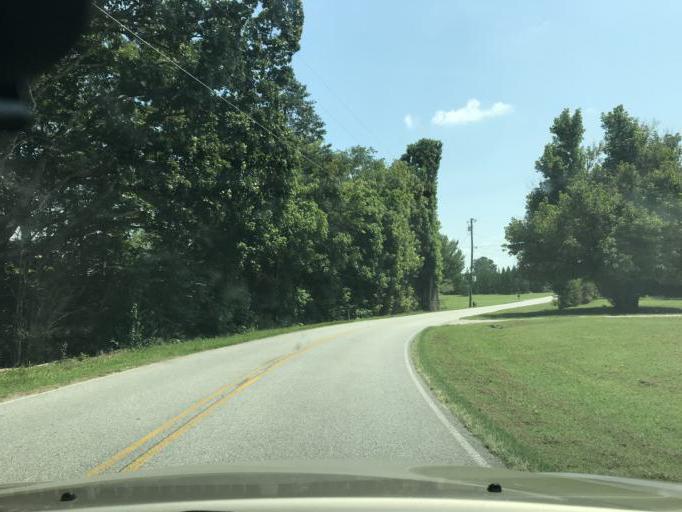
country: US
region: Georgia
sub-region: Dawson County
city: Dawsonville
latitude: 34.3341
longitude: -84.0785
